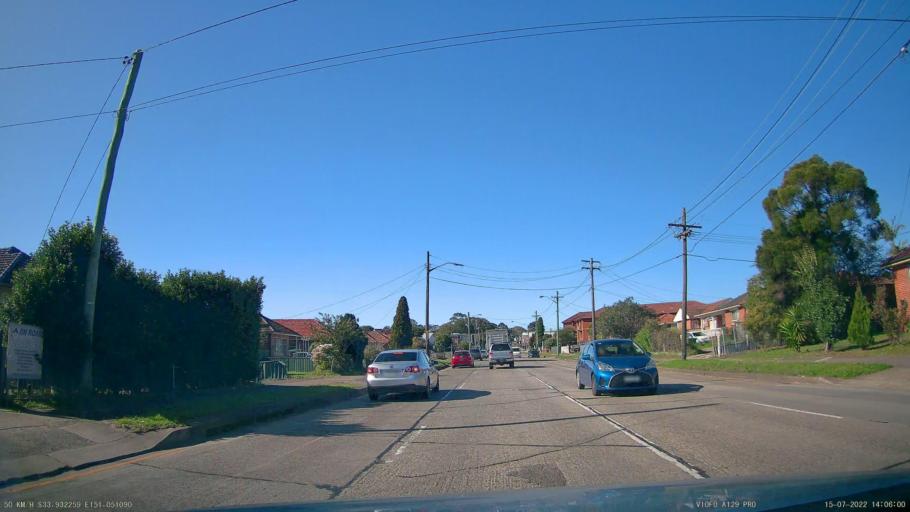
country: AU
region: New South Wales
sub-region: Canterbury
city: Roselands
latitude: -33.9322
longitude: 151.0513
